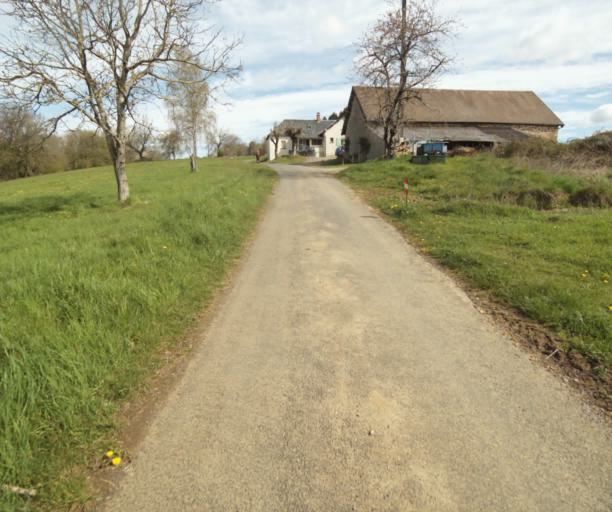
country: FR
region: Limousin
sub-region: Departement de la Correze
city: Laguenne
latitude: 45.2529
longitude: 1.8070
